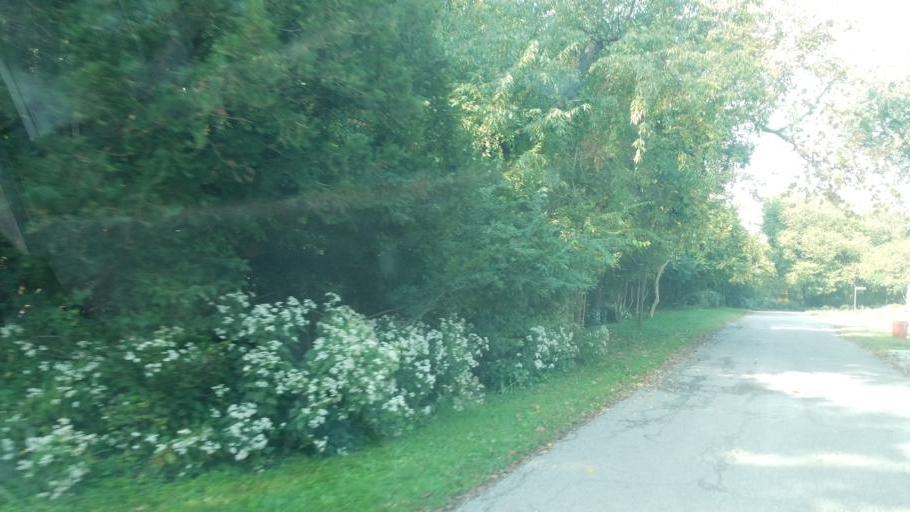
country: US
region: Ohio
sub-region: Franklin County
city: Worthington
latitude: 40.0628
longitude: -83.0270
